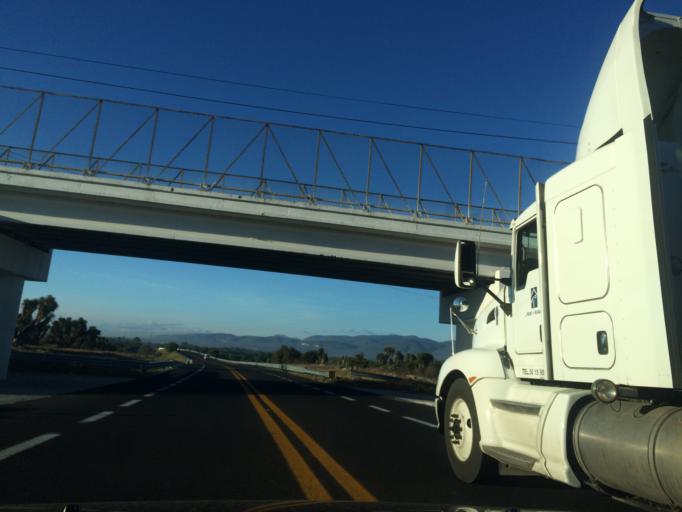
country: MX
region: Puebla
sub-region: Tehuacan
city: Magdalena Cuayucatepec
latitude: 18.5504
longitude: -97.4627
